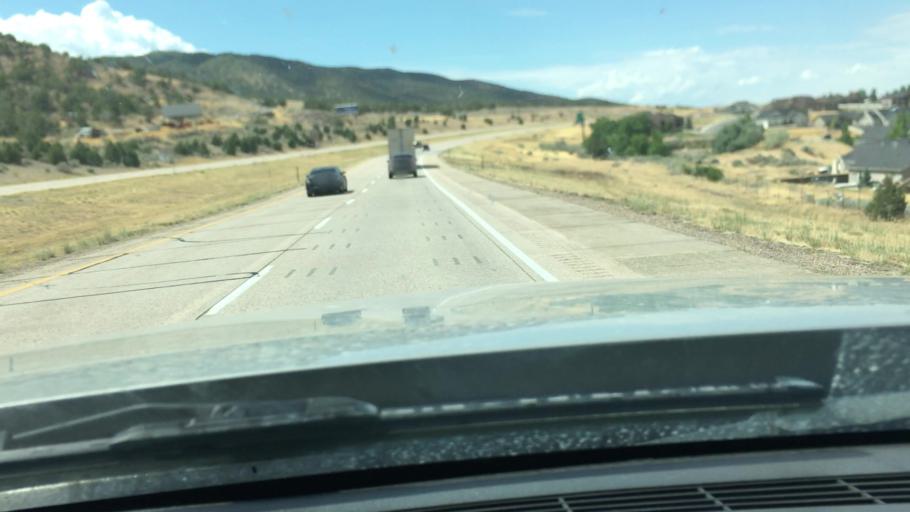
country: US
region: Utah
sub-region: Juab County
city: Nephi
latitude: 39.6981
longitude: -111.8246
